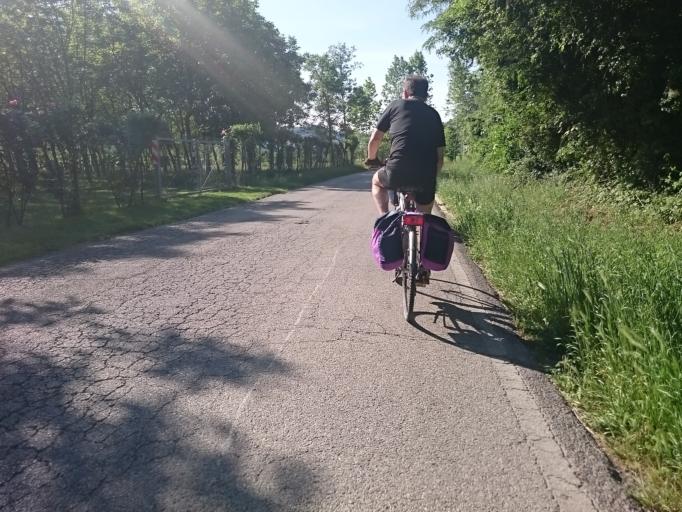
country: IT
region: Veneto
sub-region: Provincia di Padova
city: Torreglia
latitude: 45.3419
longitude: 11.7609
